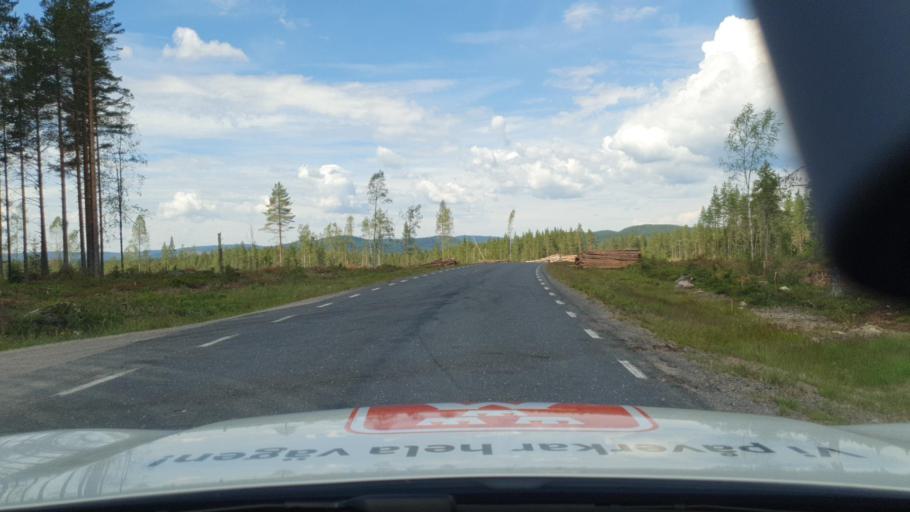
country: SE
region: Vaermland
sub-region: Torsby Kommun
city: Torsby
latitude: 60.5450
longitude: 12.7925
